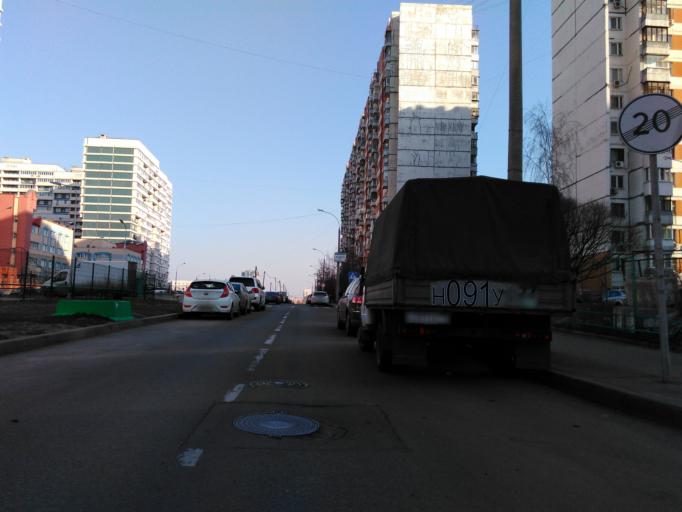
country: RU
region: Moscow
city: Ramenki
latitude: 55.6974
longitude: 37.5031
